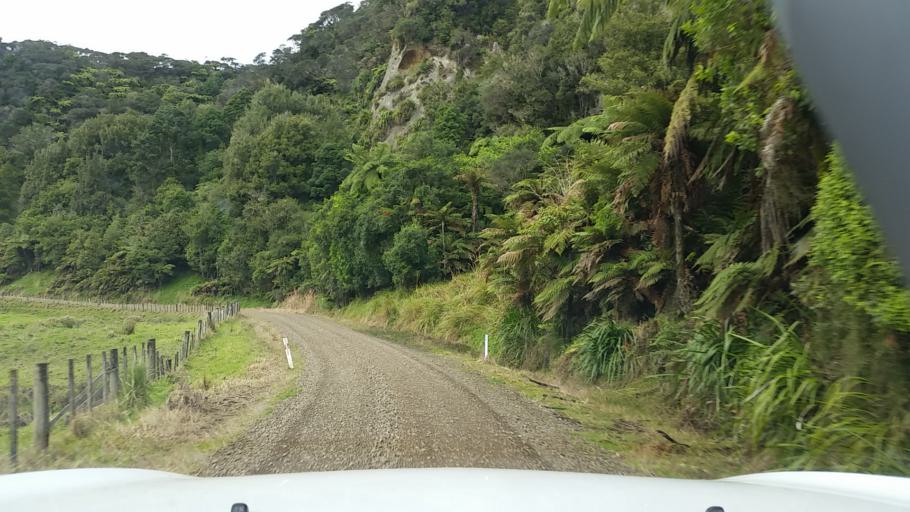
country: NZ
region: Taranaki
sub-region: New Plymouth District
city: Waitara
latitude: -38.8577
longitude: 174.6650
